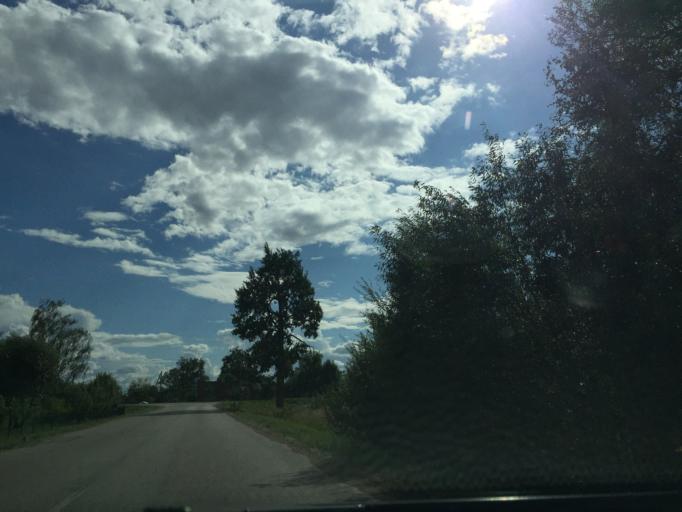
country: LT
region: Siauliu apskritis
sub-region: Joniskis
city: Joniskis
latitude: 56.2466
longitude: 23.5541
